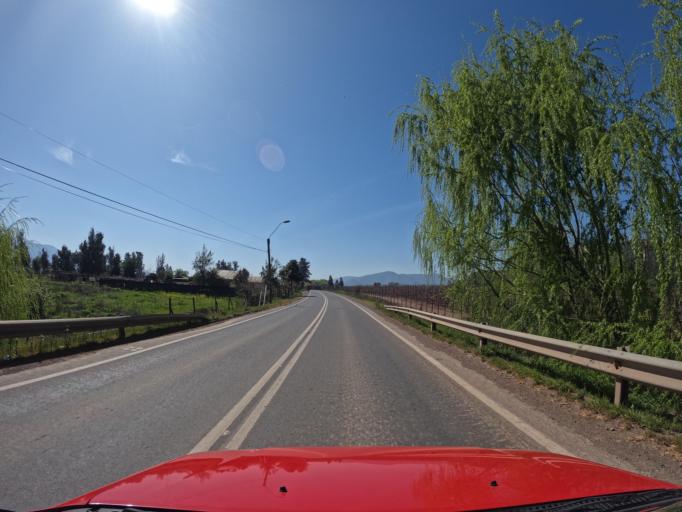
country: CL
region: Maule
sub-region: Provincia de Curico
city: Rauco
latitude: -35.0496
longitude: -71.4700
